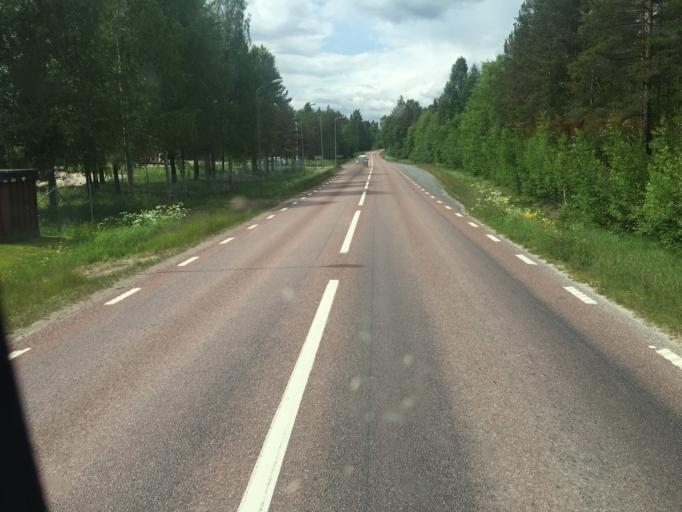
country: SE
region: Dalarna
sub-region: Vansbro Kommun
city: Vansbro
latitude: 60.5101
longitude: 14.2078
